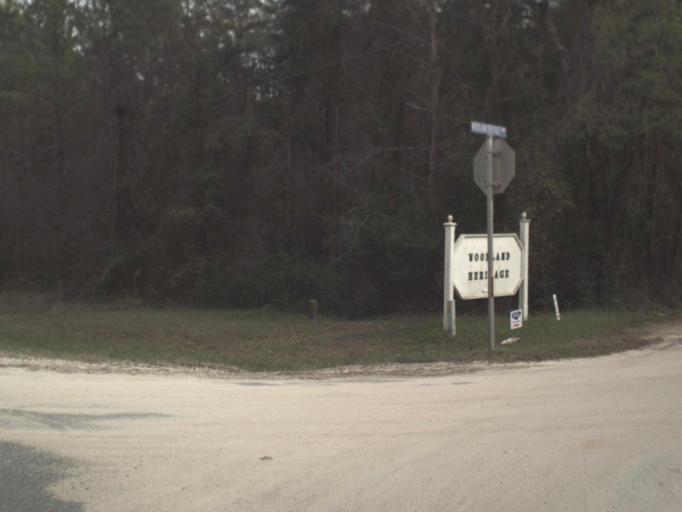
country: US
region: Florida
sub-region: Wakulla County
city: Crawfordville
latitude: 30.2550
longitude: -84.3370
